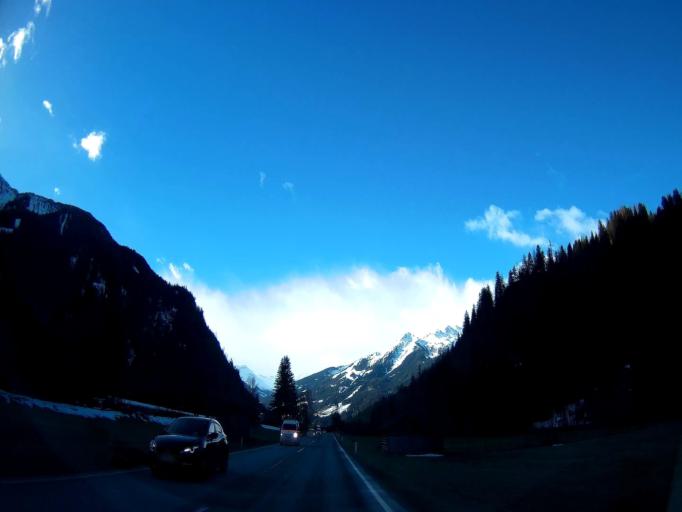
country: AT
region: Salzburg
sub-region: Politischer Bezirk Sankt Johann im Pongau
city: Dorfgastein
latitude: 47.2077
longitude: 13.1081
